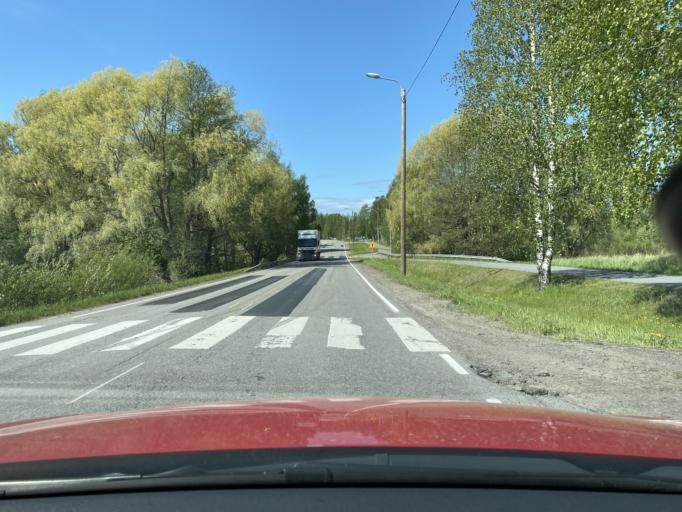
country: FI
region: Satakunta
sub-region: Rauma
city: Eura
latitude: 61.1157
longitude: 22.1519
